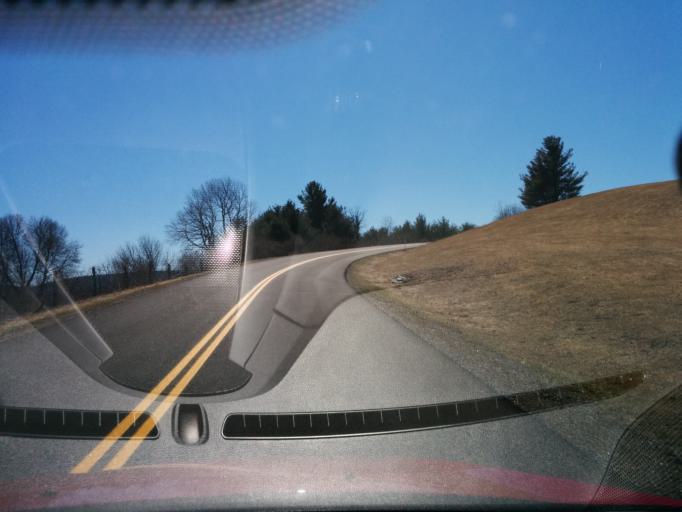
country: US
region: Virginia
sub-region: Augusta County
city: Stuarts Draft
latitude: 37.8920
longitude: -79.1362
